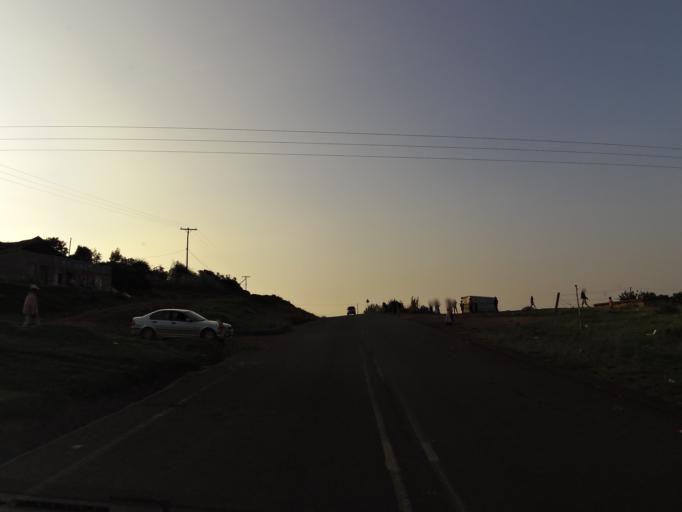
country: LS
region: Leribe
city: Leribe
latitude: -29.0285
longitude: 28.2326
